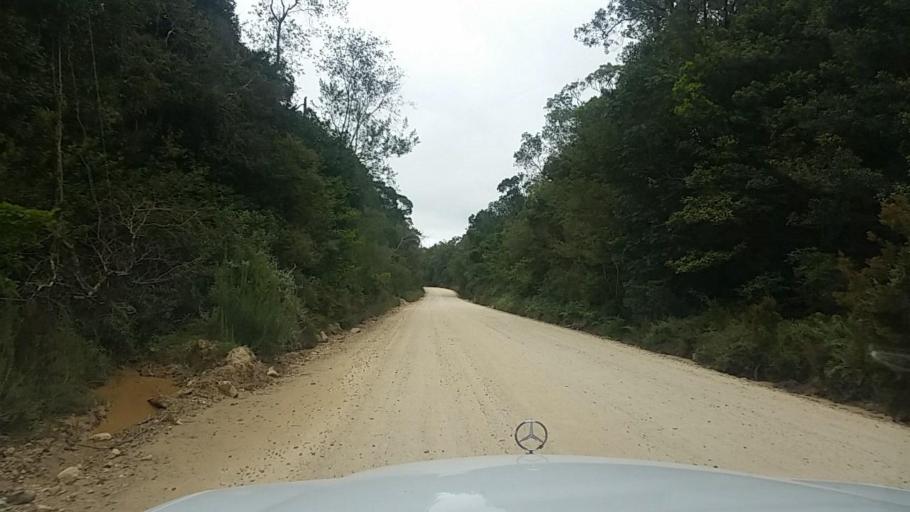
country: ZA
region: Western Cape
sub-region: Eden District Municipality
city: Knysna
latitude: -33.9628
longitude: 23.1563
